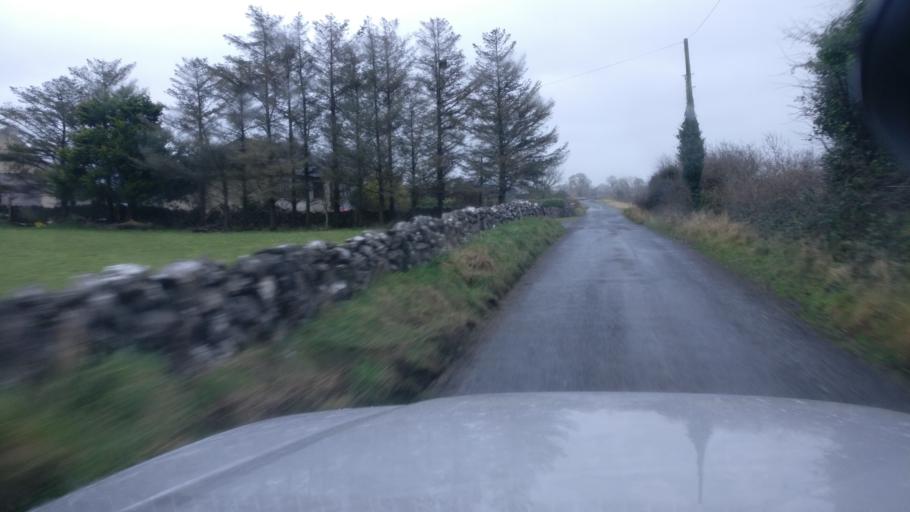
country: IE
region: Connaught
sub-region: County Galway
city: Loughrea
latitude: 53.2313
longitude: -8.5987
